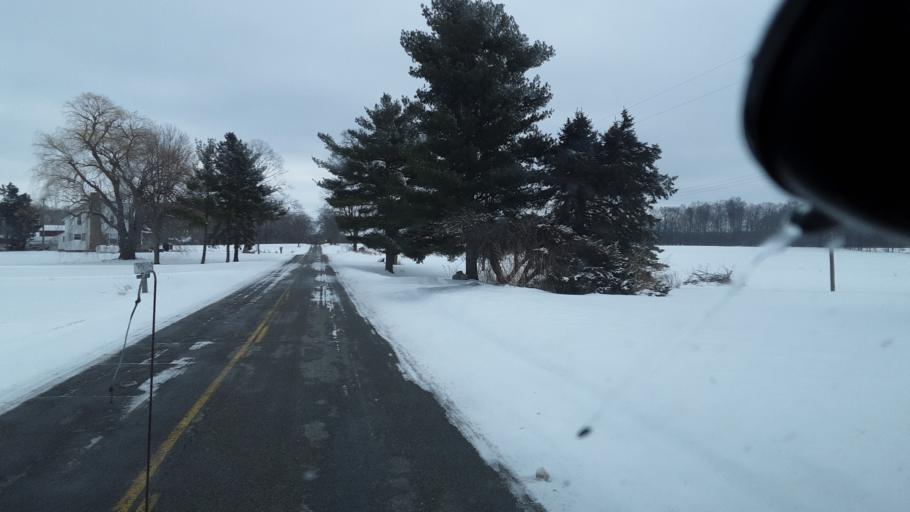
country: US
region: Michigan
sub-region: Ingham County
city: Mason
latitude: 42.5333
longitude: -84.3996
